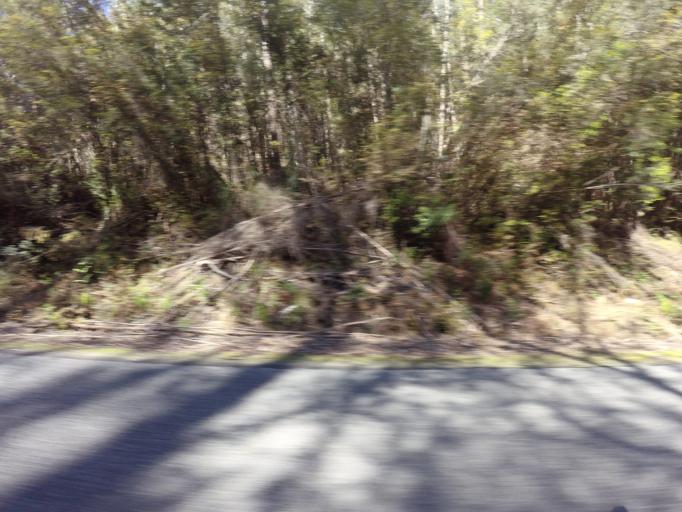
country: AU
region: Tasmania
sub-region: Derwent Valley
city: New Norfolk
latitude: -42.7462
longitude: 146.4141
